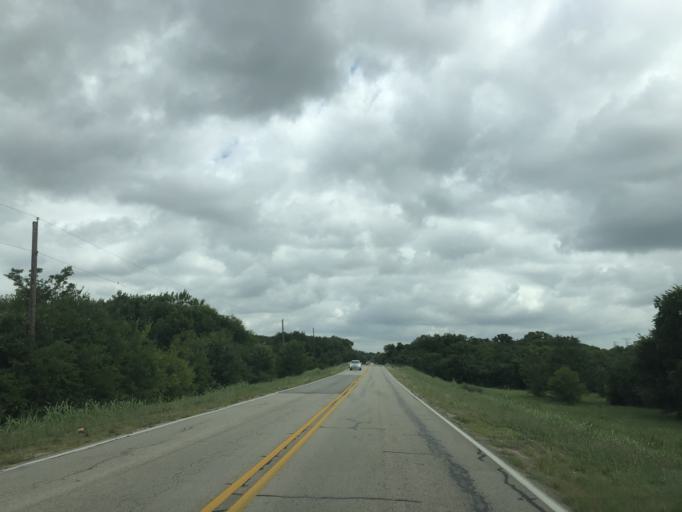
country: US
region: Texas
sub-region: Dallas County
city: Sunnyvale
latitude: 32.8160
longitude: -96.5595
